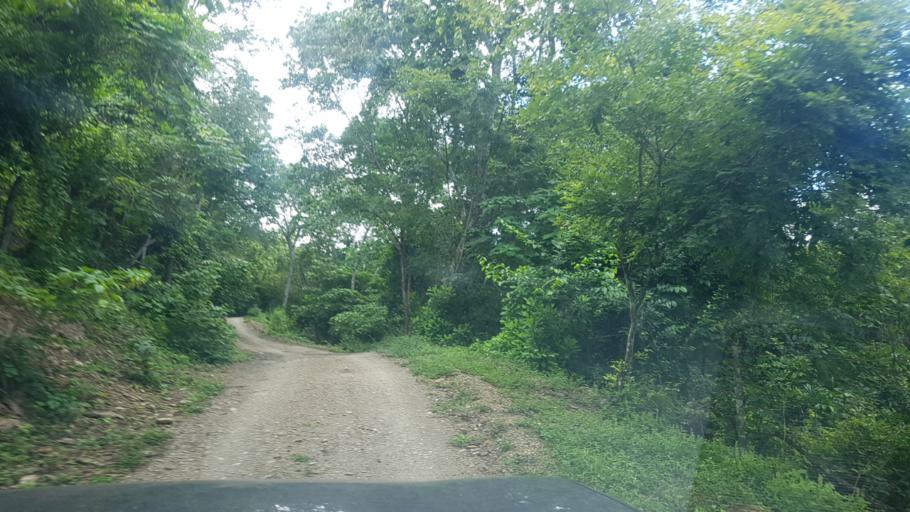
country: NI
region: Nueva Segovia
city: Ocotal
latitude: 13.5953
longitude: -86.4177
